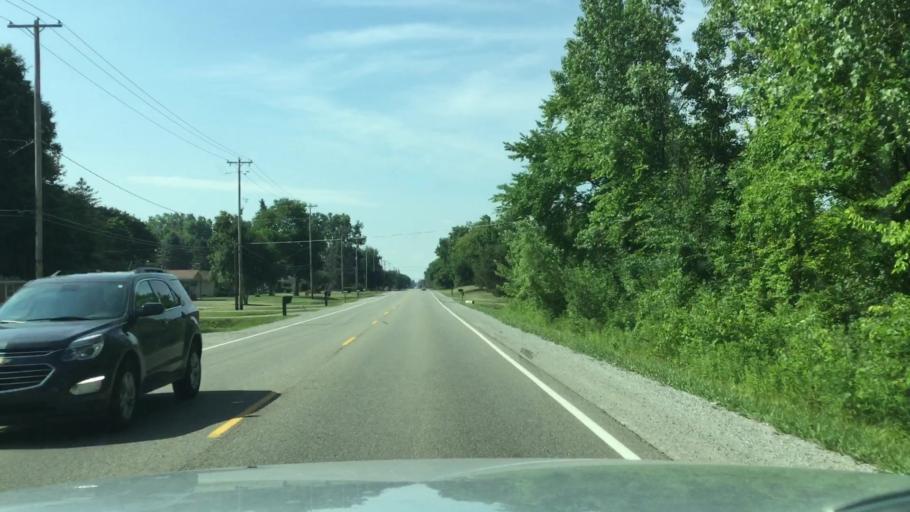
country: US
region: Michigan
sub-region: Genesee County
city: Flushing
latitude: 43.0729
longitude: -83.8134
